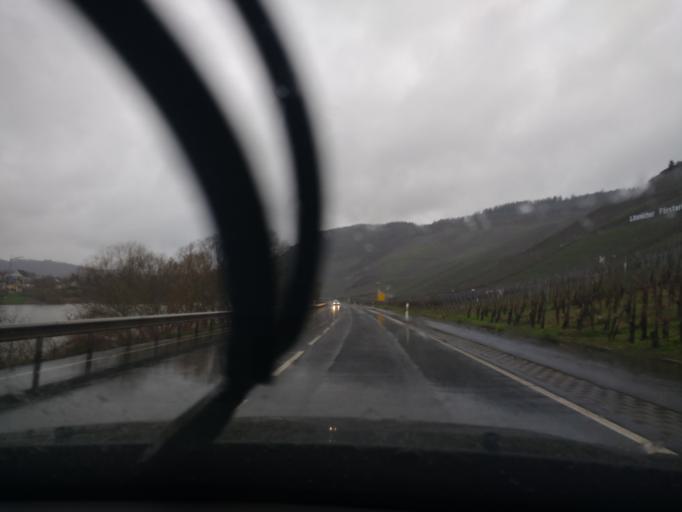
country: DE
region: Rheinland-Pfalz
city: Kinheim
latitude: 49.9766
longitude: 7.0457
